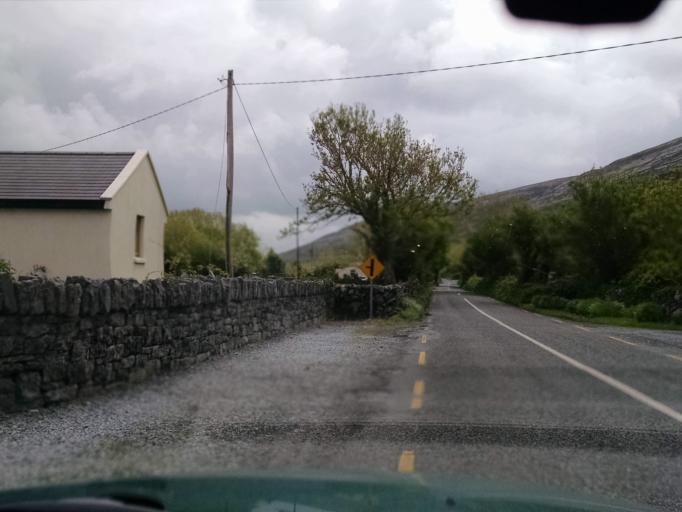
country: IE
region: Connaught
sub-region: County Galway
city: Bearna
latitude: 53.1405
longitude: -9.2256
